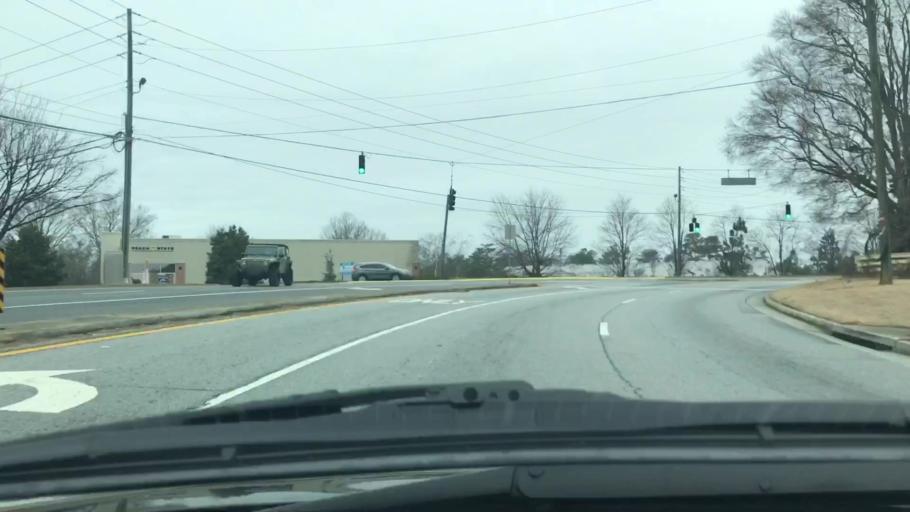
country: US
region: Georgia
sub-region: Gwinnett County
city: Norcross
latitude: 33.9554
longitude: -84.2074
